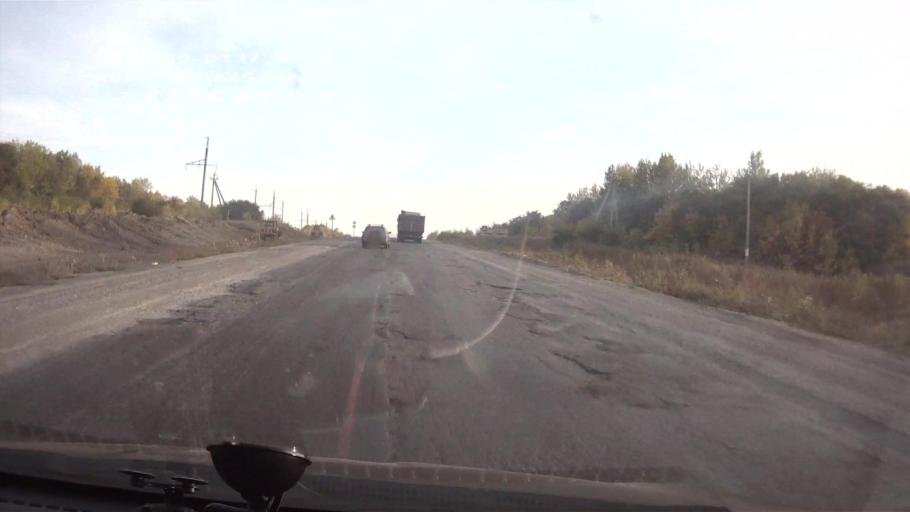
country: RU
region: Saratov
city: Krasnoarmeysk
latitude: 51.1906
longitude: 45.6481
